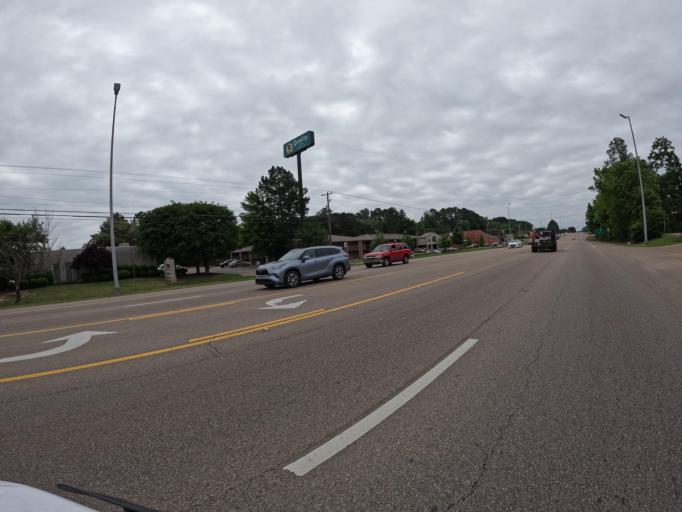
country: US
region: Mississippi
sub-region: Lee County
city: Tupelo
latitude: 34.2799
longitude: -88.7157
